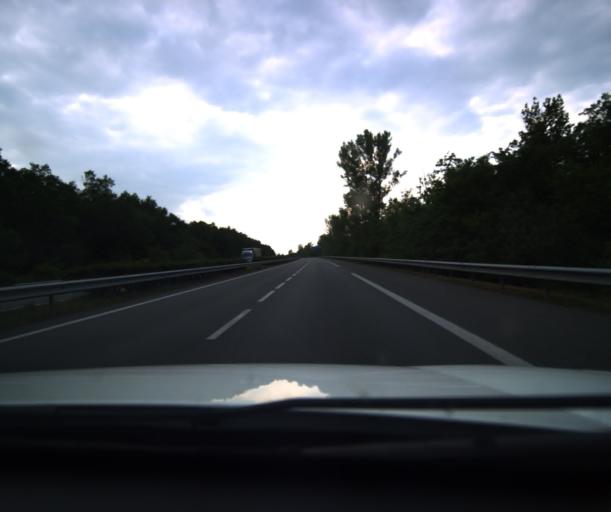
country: FR
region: Midi-Pyrenees
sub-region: Departement du Tarn-et-Garonne
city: Saint-Porquier
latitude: 44.0112
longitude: 1.2107
